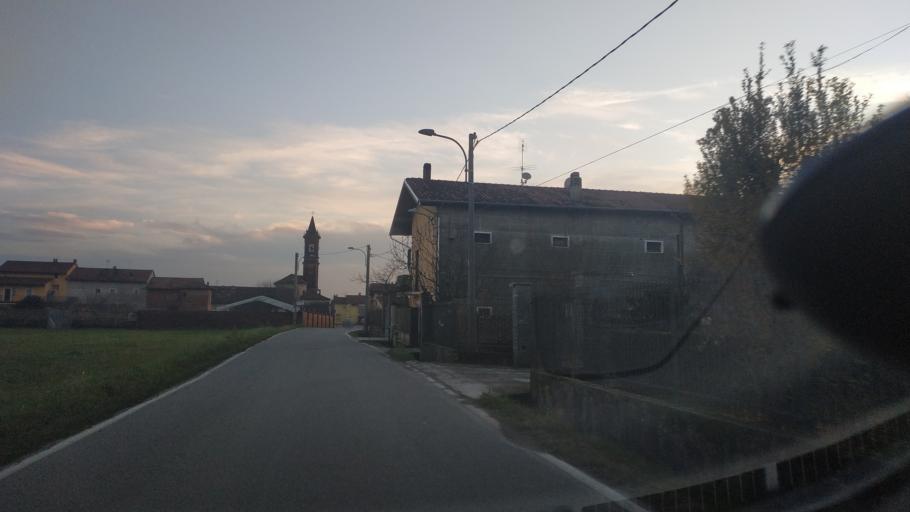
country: IT
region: Piedmont
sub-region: Provincia di Torino
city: Caluso
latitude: 45.2682
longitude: 7.8782
